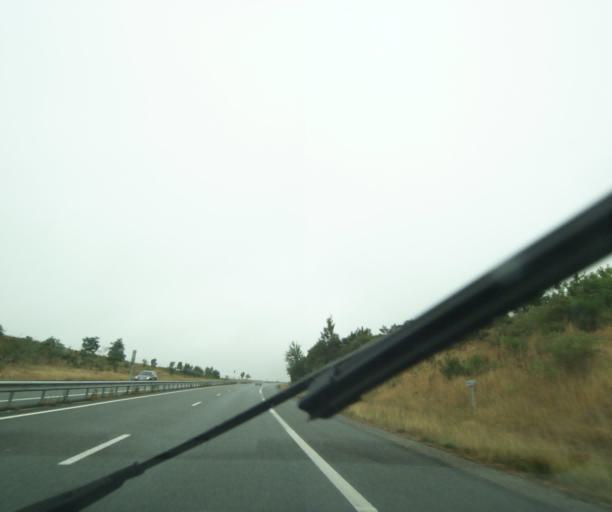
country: FR
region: Midi-Pyrenees
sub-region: Departement de l'Aveyron
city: Naucelle
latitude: 44.1269
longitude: 2.3084
